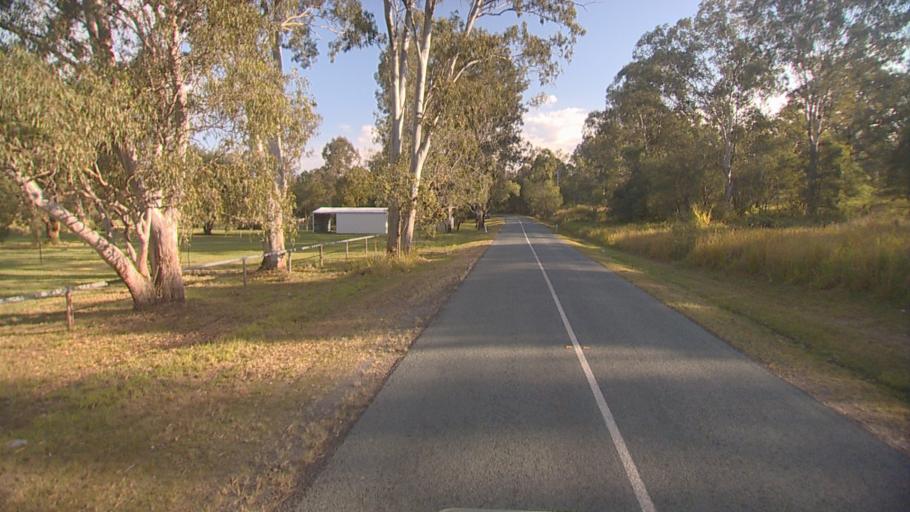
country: AU
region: Queensland
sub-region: Gold Coast
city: Ormeau Hills
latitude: -27.8249
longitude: 153.1768
